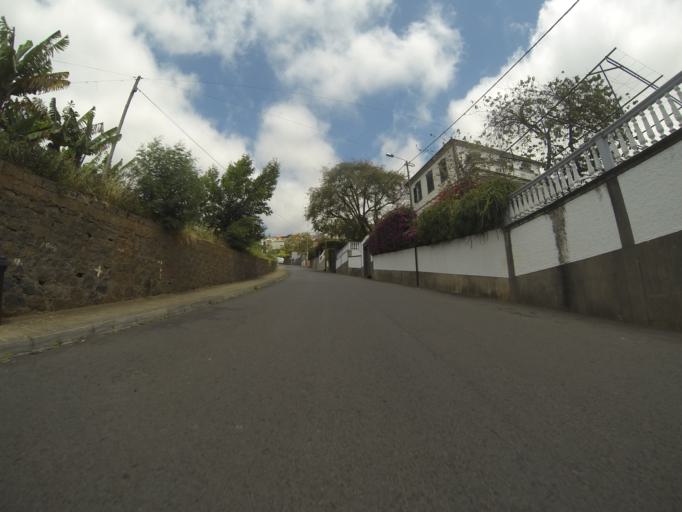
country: PT
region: Madeira
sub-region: Funchal
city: Nossa Senhora do Monte
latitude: 32.6661
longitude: -16.9318
